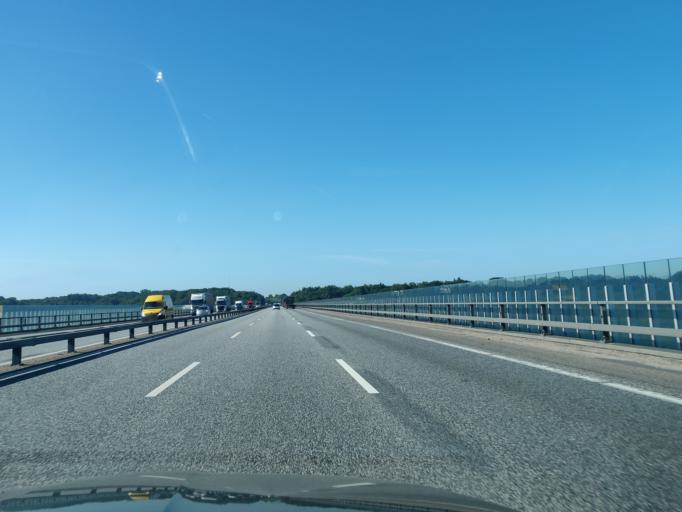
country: DK
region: South Denmark
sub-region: Vejle Kommune
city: Vejle
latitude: 55.6983
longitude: 9.5722
